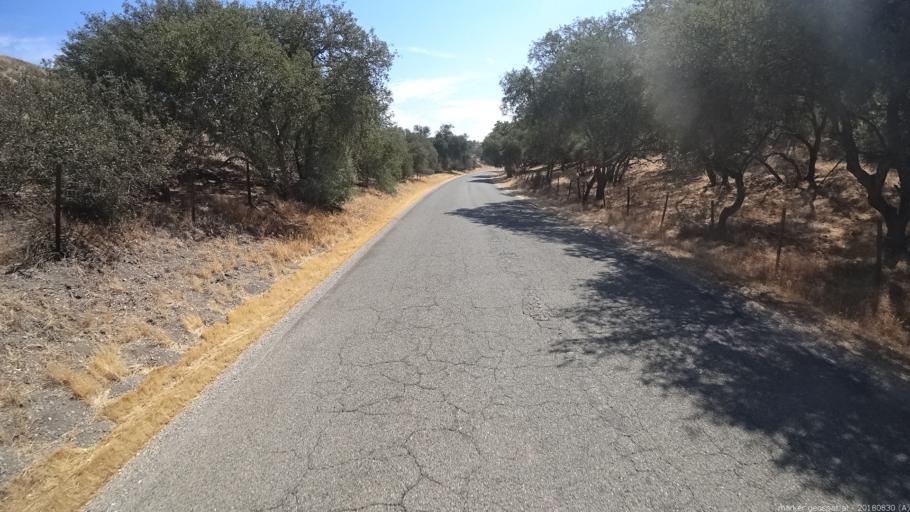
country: US
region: California
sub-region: Monterey County
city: King City
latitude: 36.1152
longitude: -121.1167
